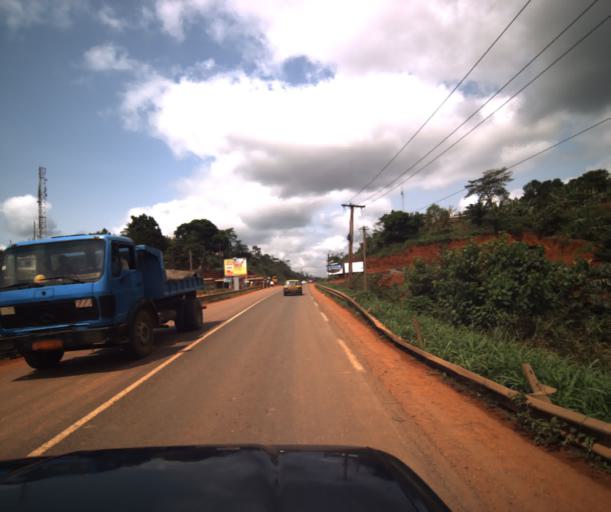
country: CM
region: Centre
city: Yaounde
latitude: 3.7962
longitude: 11.4977
